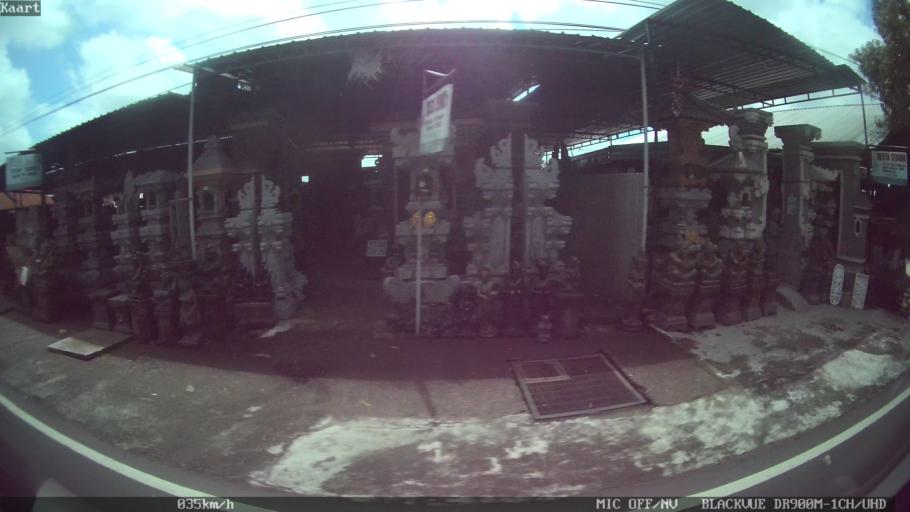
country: ID
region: Bali
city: Banjar Sedang
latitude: -8.5653
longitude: 115.2815
